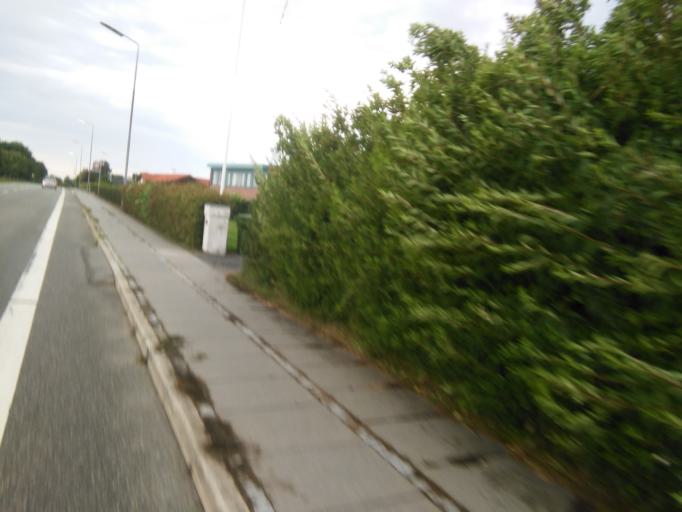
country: DK
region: Central Jutland
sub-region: Arhus Kommune
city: Hjortshoj
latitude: 56.2161
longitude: 10.2914
